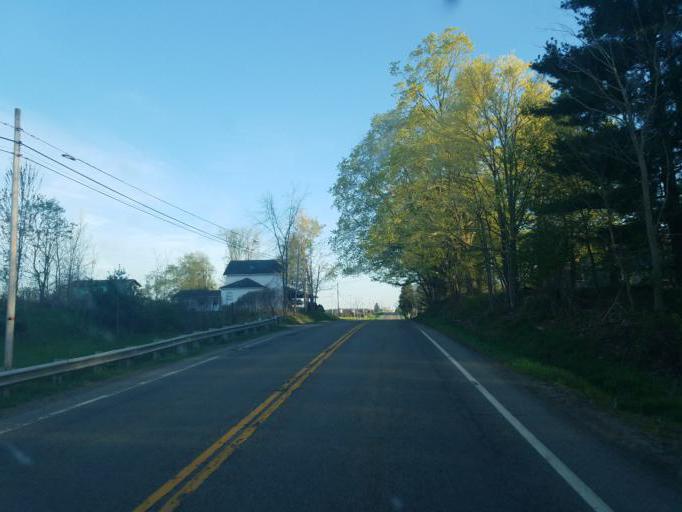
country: US
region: Ohio
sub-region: Ashtabula County
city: Andover
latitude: 41.6771
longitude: -80.5704
